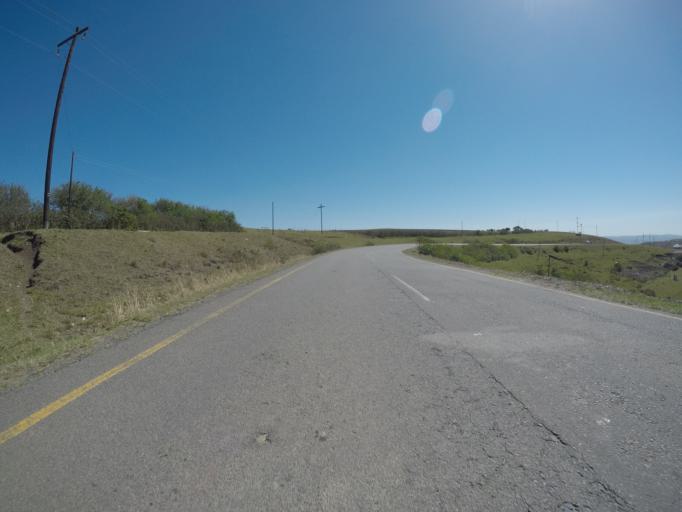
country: ZA
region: Eastern Cape
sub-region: OR Tambo District Municipality
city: Libode
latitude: -31.9140
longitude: 28.9826
